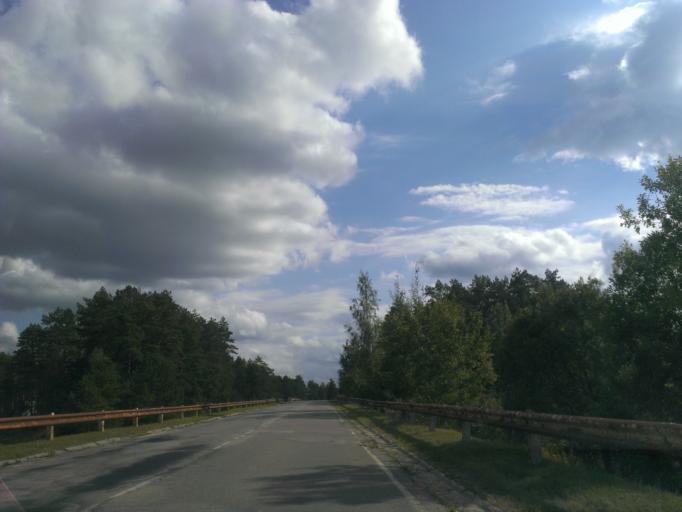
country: LV
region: Incukalns
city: Vangazi
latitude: 57.0821
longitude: 24.5200
